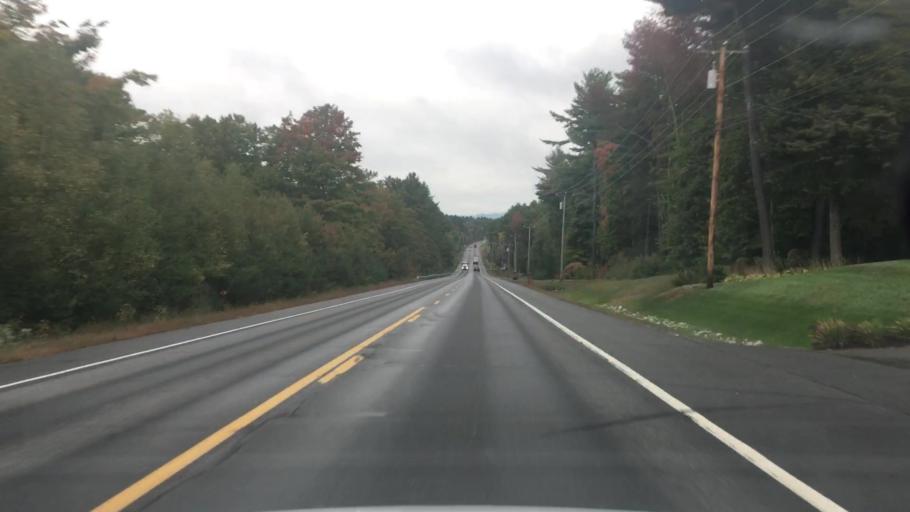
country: US
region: Maine
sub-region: Kennebec County
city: Belgrade
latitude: 44.3986
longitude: -69.8060
